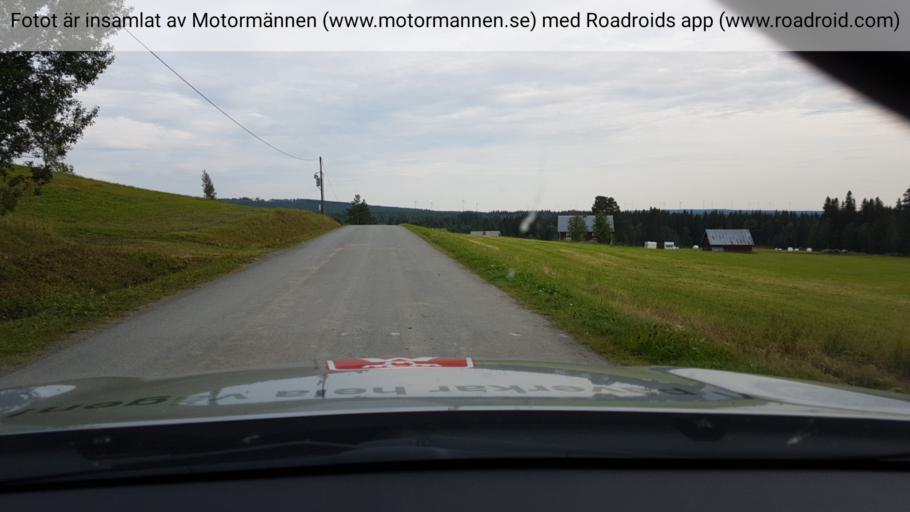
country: SE
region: Jaemtland
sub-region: OEstersunds Kommun
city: Lit
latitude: 63.6421
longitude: 14.9562
